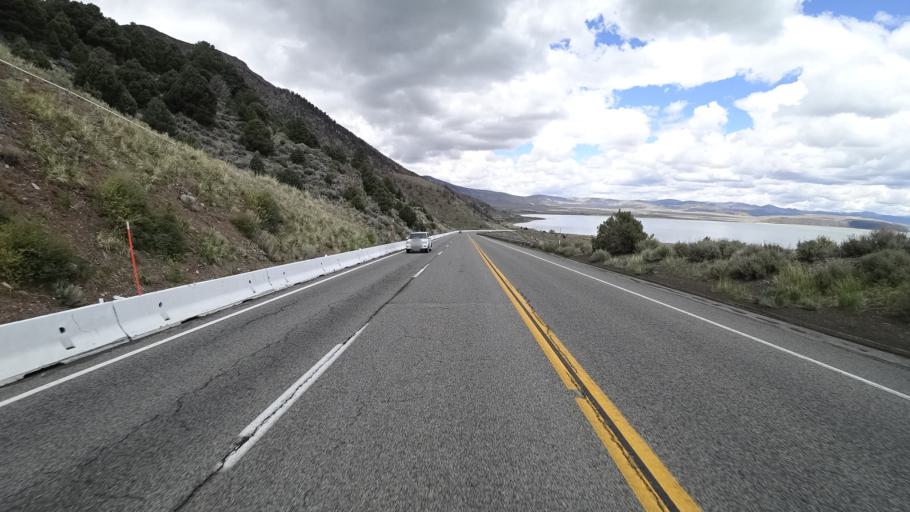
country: US
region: California
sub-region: Mono County
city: Bridgeport
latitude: 37.9701
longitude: -119.1321
